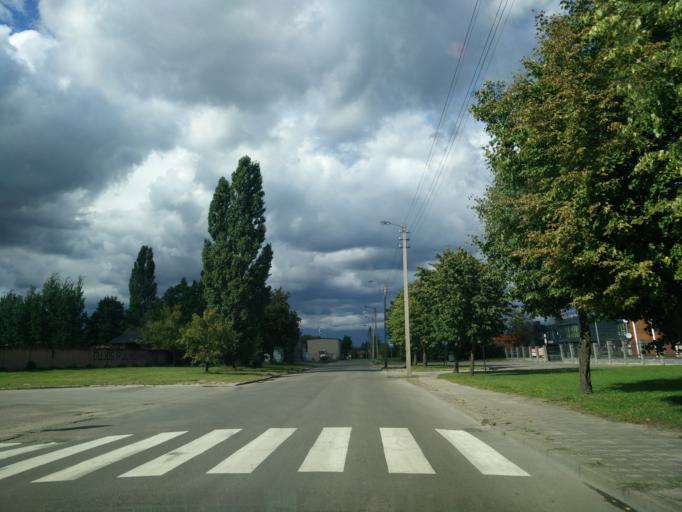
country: LT
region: Kauno apskritis
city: Dainava (Kaunas)
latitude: 54.9089
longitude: 24.0097
